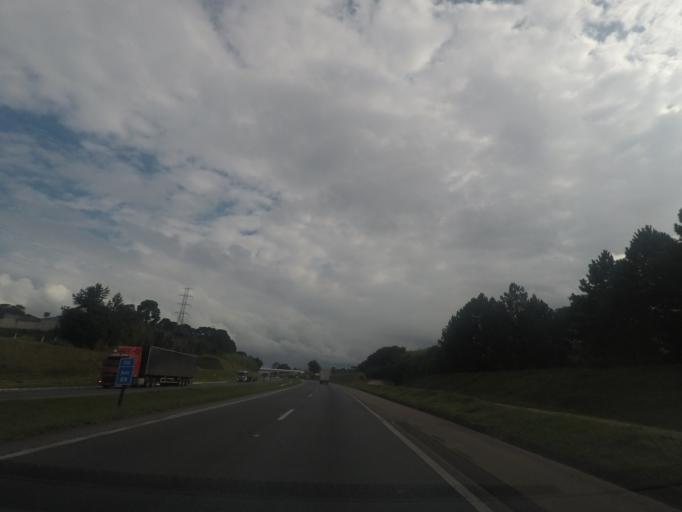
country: BR
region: Parana
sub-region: Piraquara
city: Piraquara
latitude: -25.4827
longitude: -49.1064
